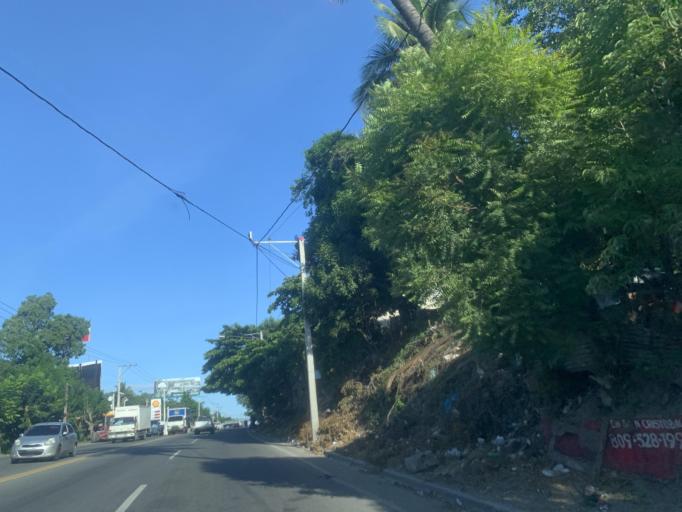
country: DO
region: San Cristobal
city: El Carril
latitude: 18.4352
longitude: -70.0126
